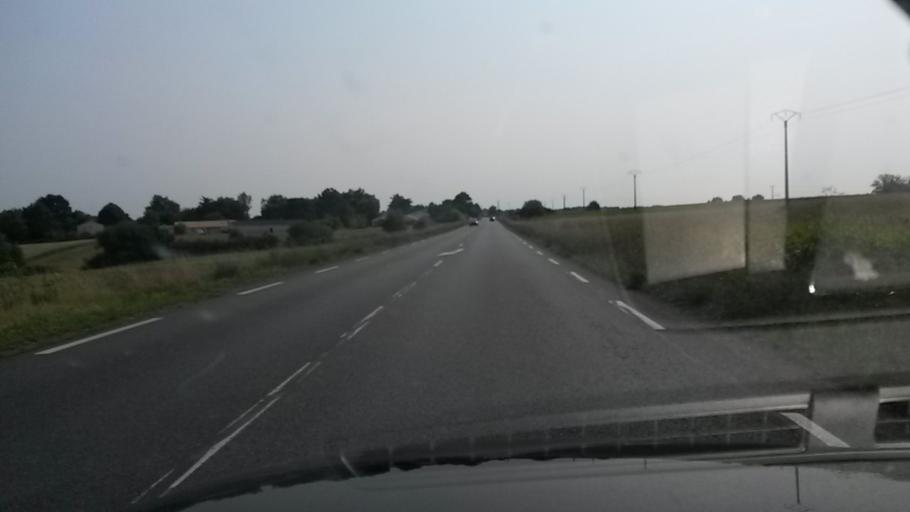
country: FR
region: Pays de la Loire
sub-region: Departement de la Loire-Atlantique
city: Mouzillon
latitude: 47.1496
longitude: -1.2797
